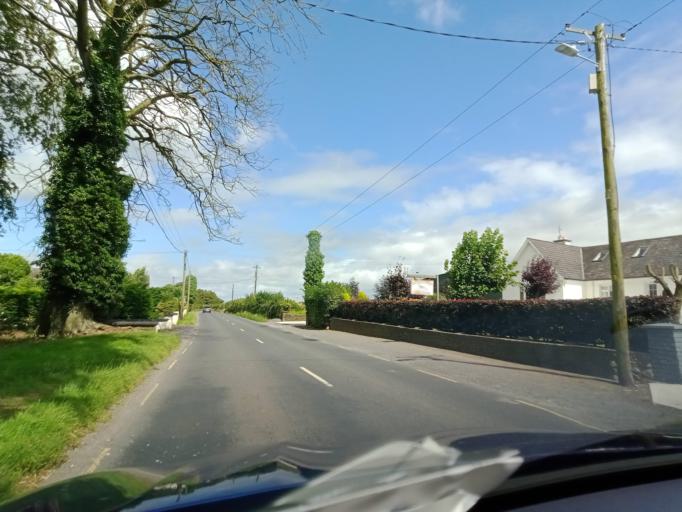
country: IE
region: Leinster
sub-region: Laois
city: Portlaoise
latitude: 52.9573
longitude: -7.3000
